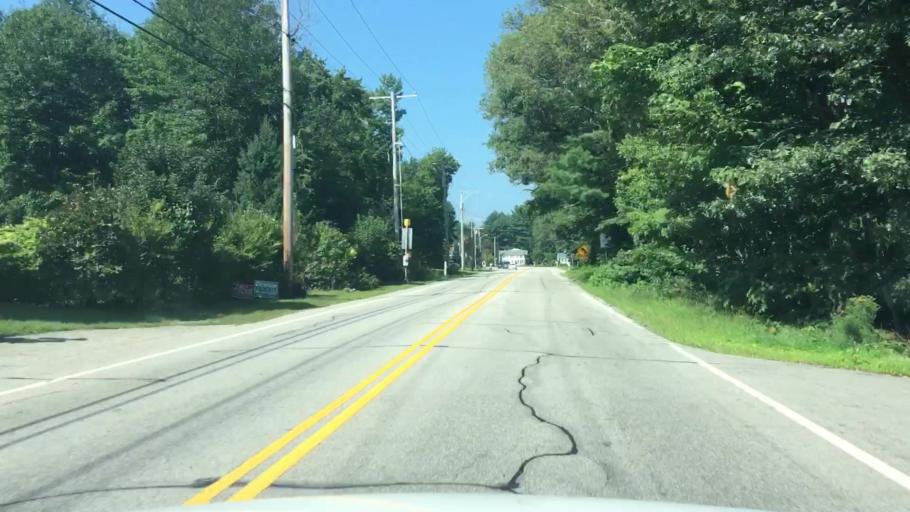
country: US
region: New Hampshire
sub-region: Rockingham County
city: Kingston
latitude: 42.9109
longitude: -71.0764
